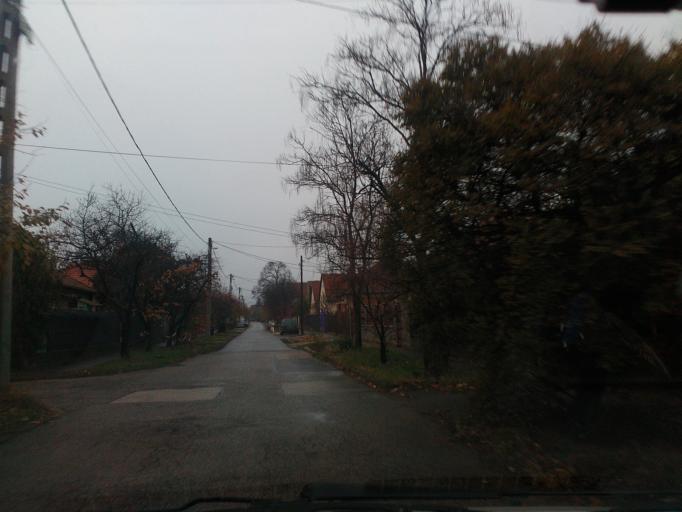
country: HU
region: Pest
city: Gyal
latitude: 47.4345
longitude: 19.2263
